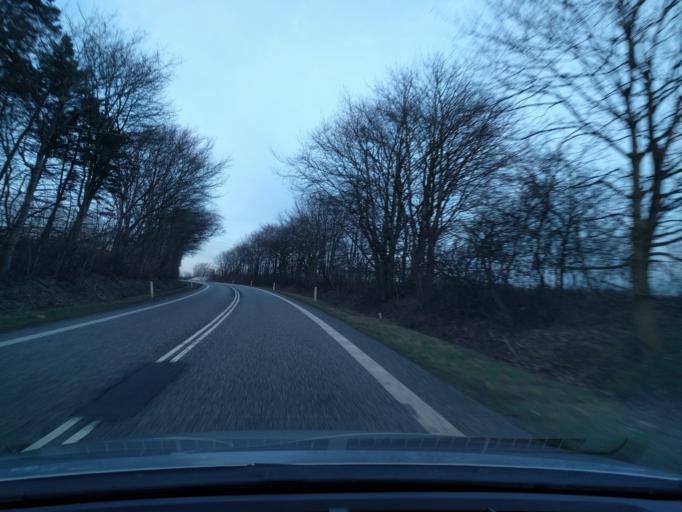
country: DK
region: South Denmark
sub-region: Tonder Kommune
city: Logumkloster
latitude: 55.1306
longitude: 8.9991
